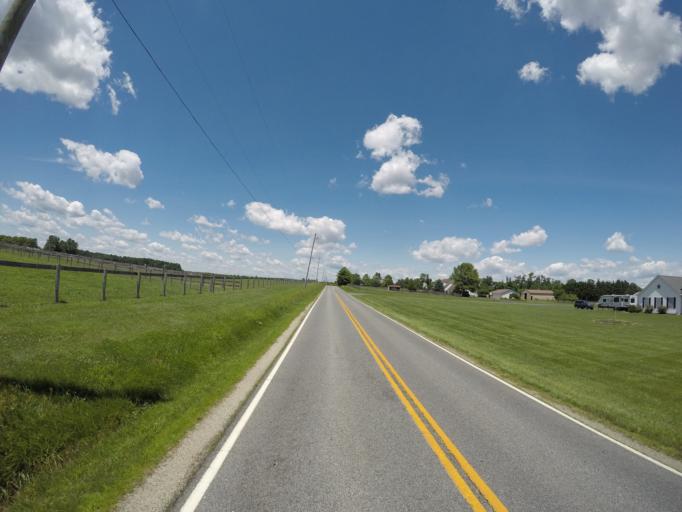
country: US
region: Delaware
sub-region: New Castle County
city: Middletown
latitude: 39.4736
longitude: -75.7793
